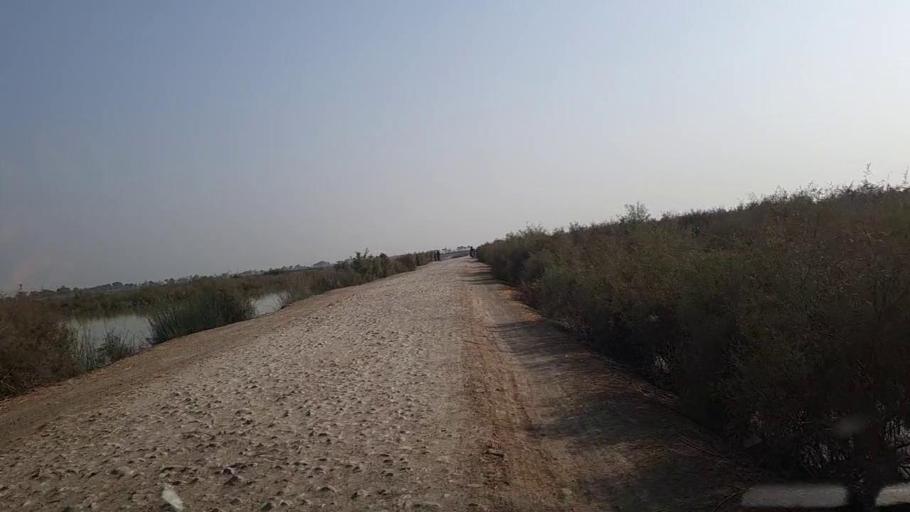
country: PK
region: Sindh
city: Kandhkot
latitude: 28.2940
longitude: 69.2530
